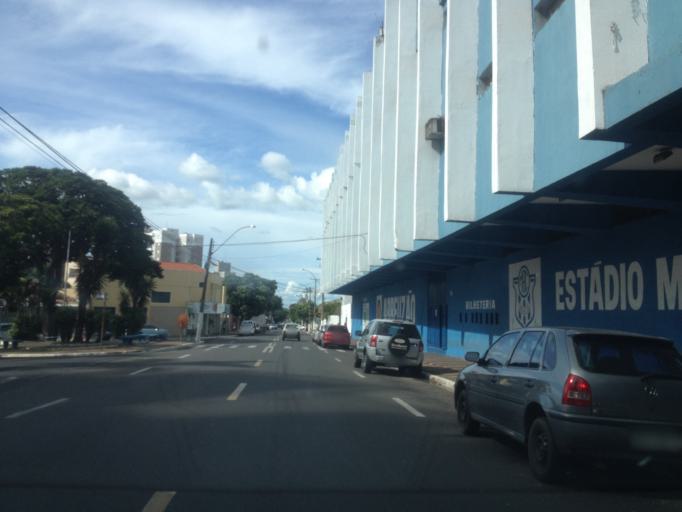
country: BR
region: Sao Paulo
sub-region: Marilia
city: Marilia
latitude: -22.2195
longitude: -49.9400
